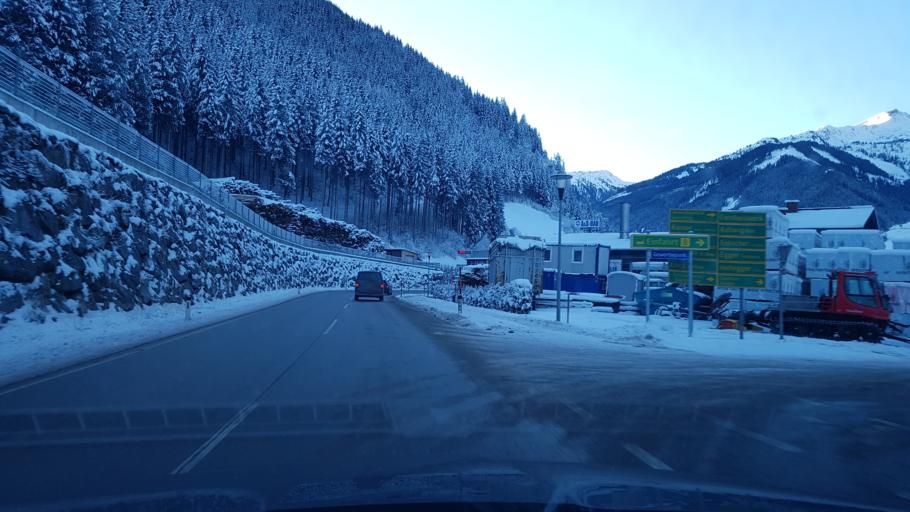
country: AT
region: Salzburg
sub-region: Politischer Bezirk Sankt Johann im Pongau
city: Huttschlag
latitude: 47.2294
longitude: 13.1990
